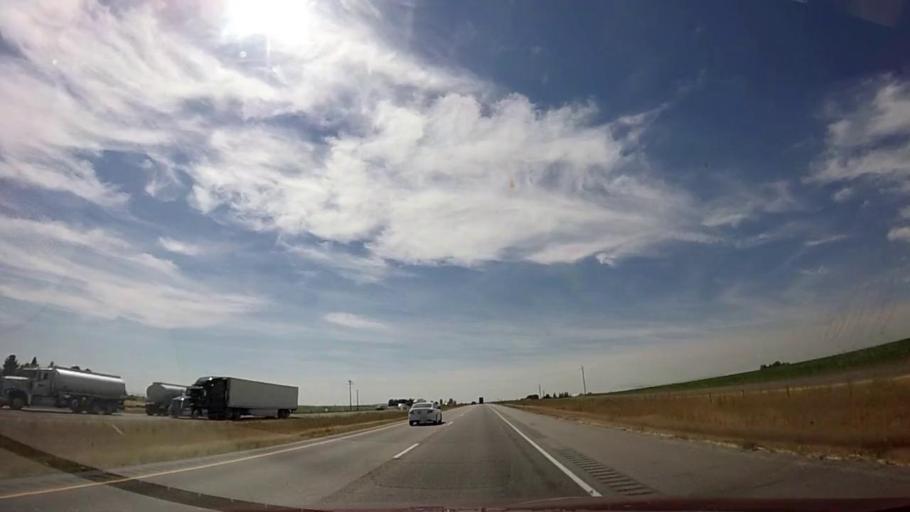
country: US
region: Idaho
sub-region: Cassia County
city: Burley
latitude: 42.5764
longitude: -113.9794
